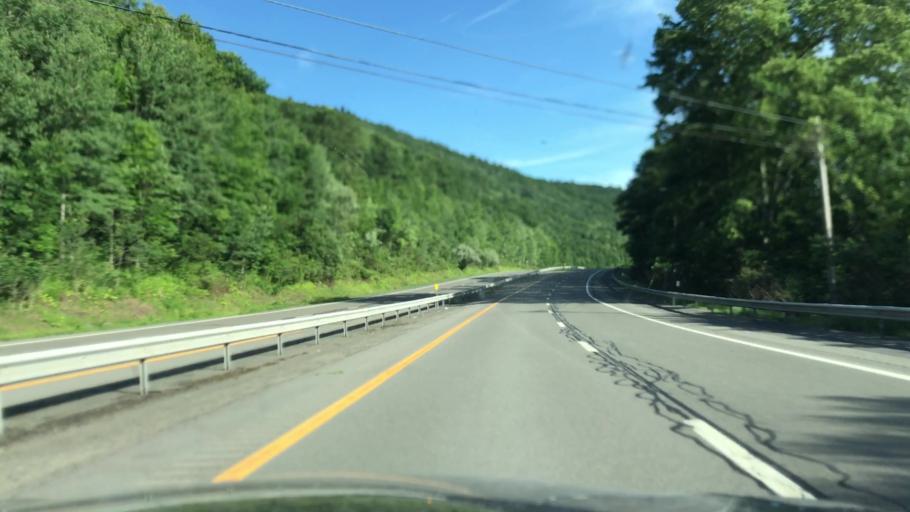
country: US
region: New York
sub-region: Delaware County
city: Hancock
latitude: 41.9925
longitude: -75.3394
